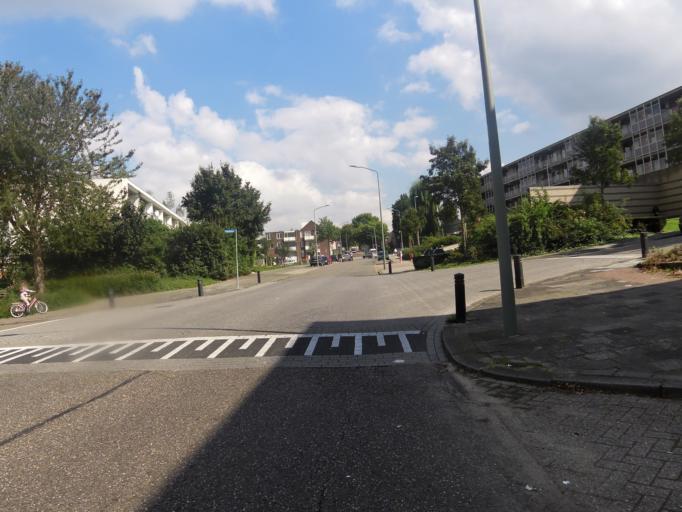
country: NL
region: Limburg
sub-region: Gemeente Brunssum
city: Brunssum
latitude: 50.9236
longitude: 5.9684
